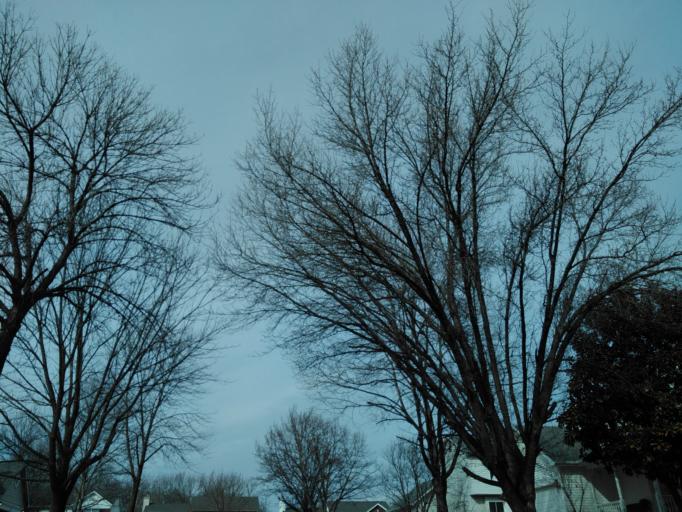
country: US
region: Missouri
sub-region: Saint Louis County
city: Valley Park
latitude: 38.5497
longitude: -90.5166
